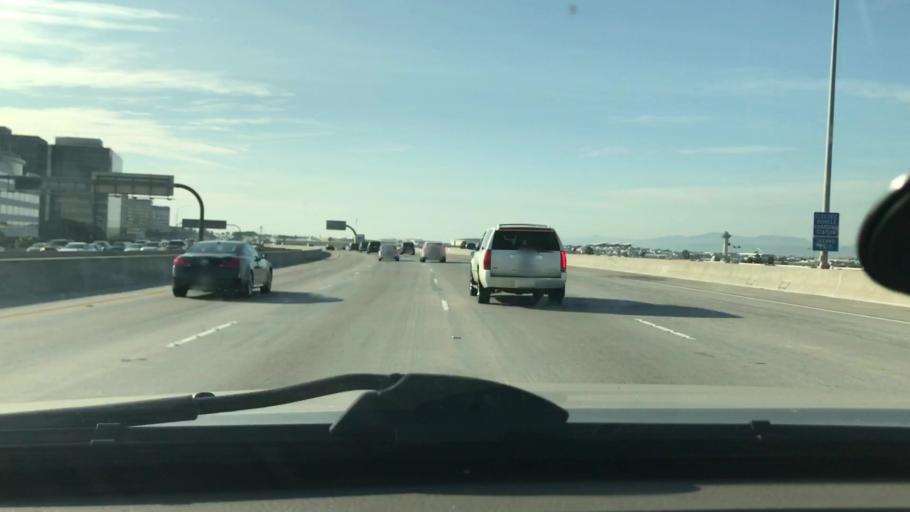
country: US
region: California
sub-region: Los Angeles County
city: Del Aire
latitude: 33.9310
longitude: -118.3794
